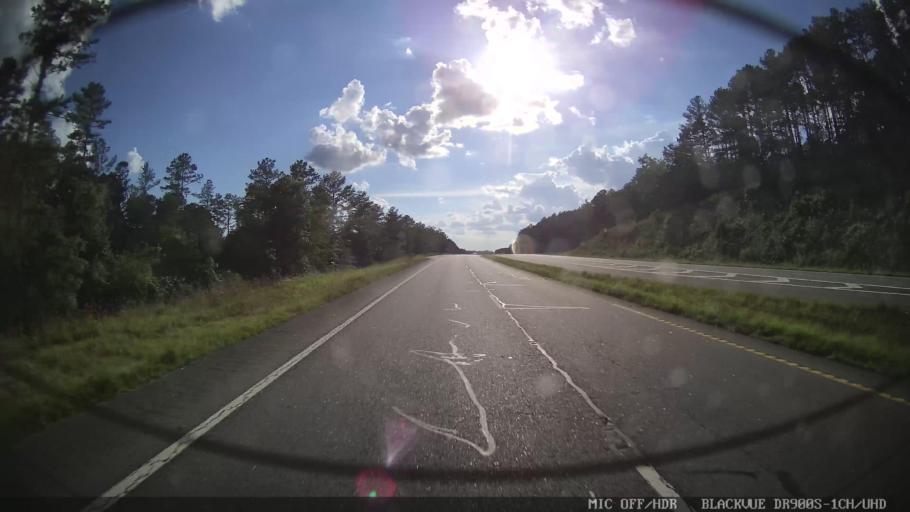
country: US
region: Georgia
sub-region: Bartow County
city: Euharlee
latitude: 34.2034
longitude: -85.0206
